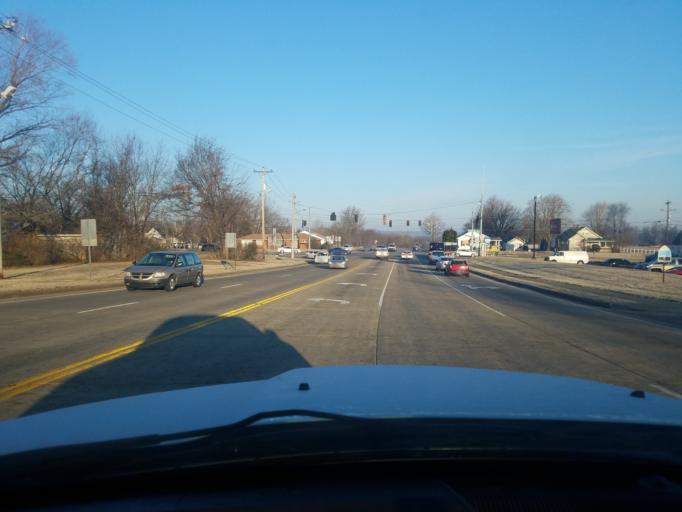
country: US
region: Kentucky
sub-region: Warren County
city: Bowling Green
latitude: 36.9679
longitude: -86.4799
